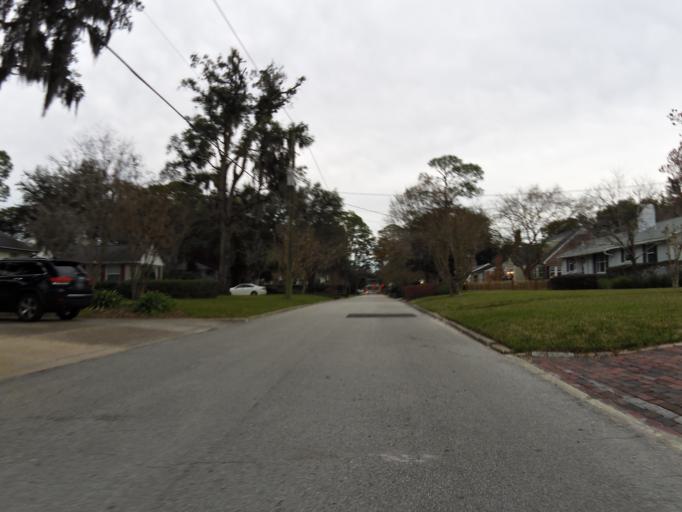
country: US
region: Florida
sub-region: Duval County
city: Jacksonville
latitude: 30.2846
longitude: -81.6535
